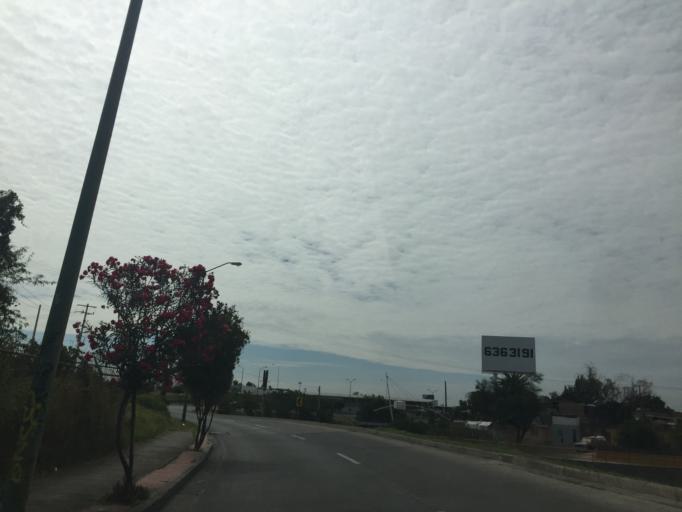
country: MX
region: Guanajuato
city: Leon
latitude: 21.1519
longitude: -101.6781
